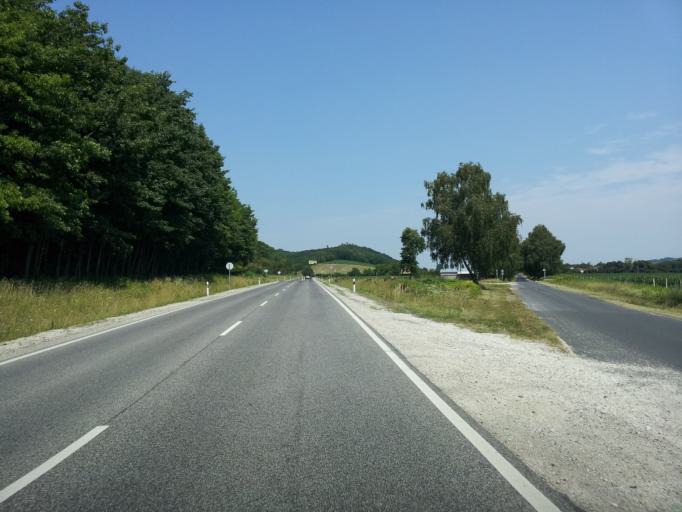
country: HU
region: Zala
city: Zalaegerszeg
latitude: 46.8364
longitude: 16.9281
